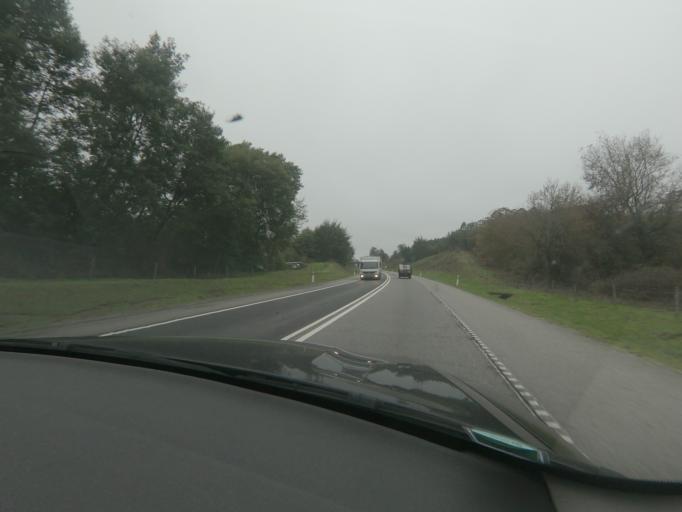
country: PT
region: Viseu
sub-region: Concelho de Tondela
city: Tondela
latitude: 40.5770
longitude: -8.0300
